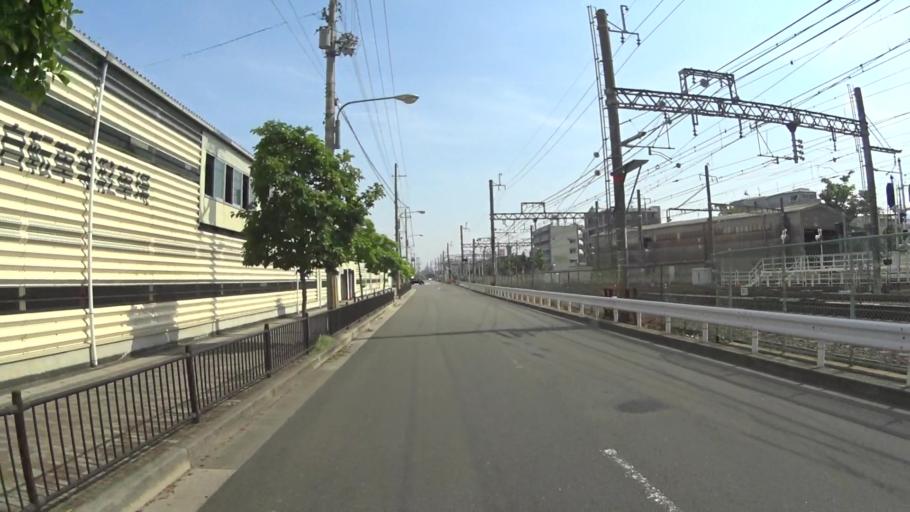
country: JP
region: Kyoto
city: Muko
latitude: 34.9776
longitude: 135.7033
